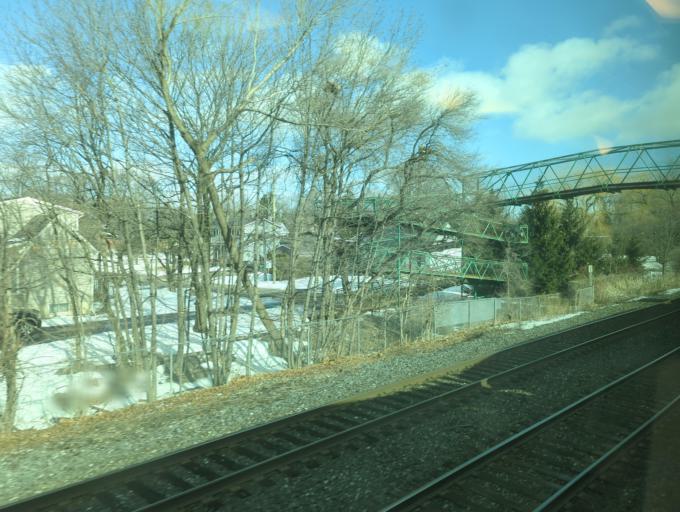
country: CA
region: Ontario
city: Burlington
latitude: 43.3434
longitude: -79.8055
